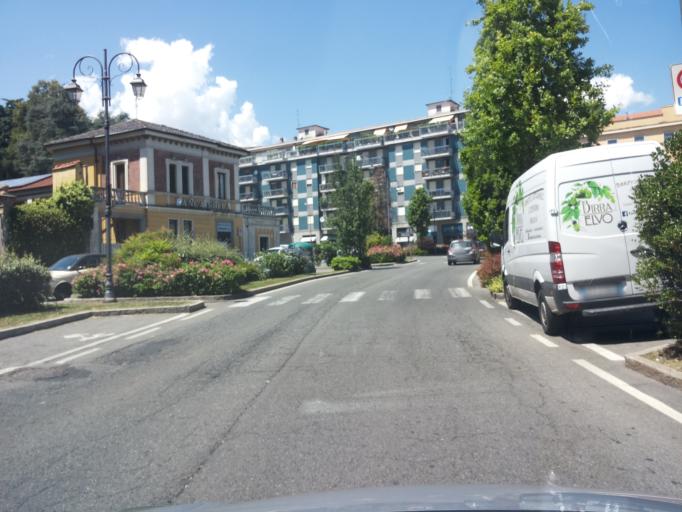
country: IT
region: Piedmont
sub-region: Provincia di Biella
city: Biella
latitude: 45.5678
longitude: 8.0505
